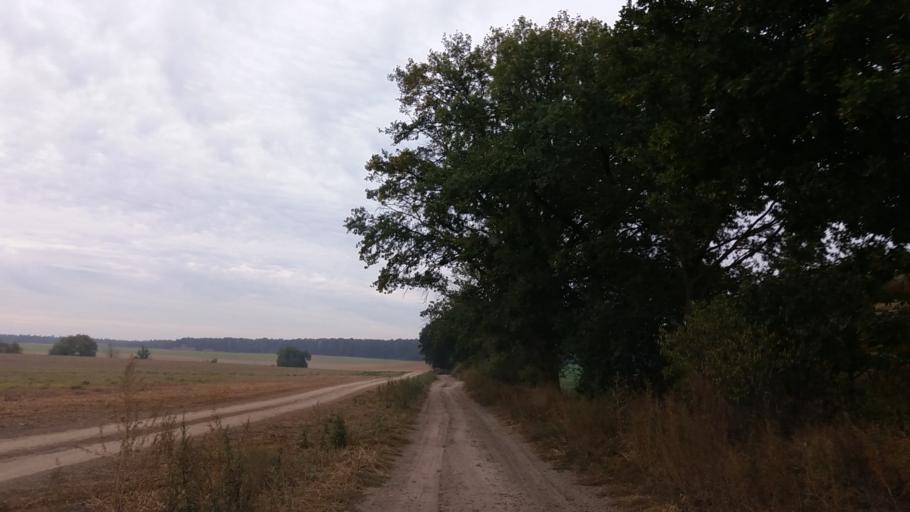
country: PL
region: West Pomeranian Voivodeship
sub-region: Powiat choszczenski
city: Pelczyce
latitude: 53.0848
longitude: 15.2968
